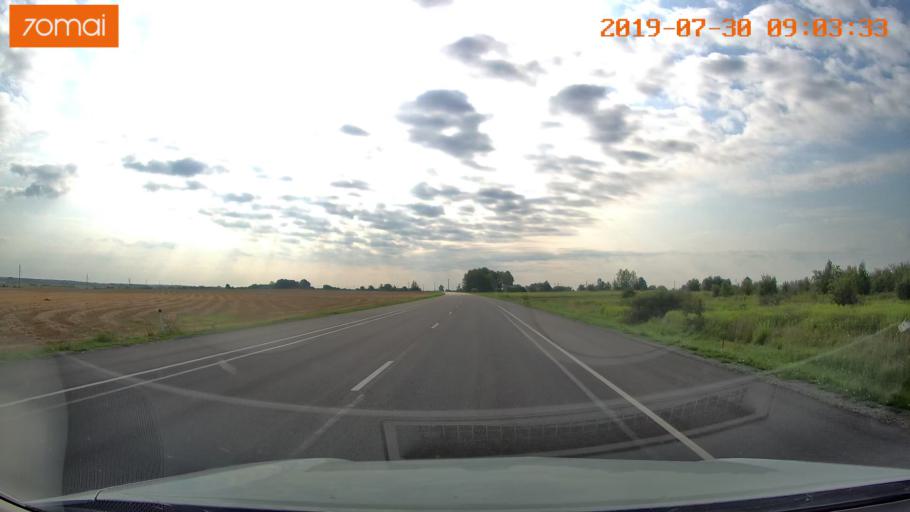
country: RU
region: Kaliningrad
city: Gusev
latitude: 54.6072
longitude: 22.2561
